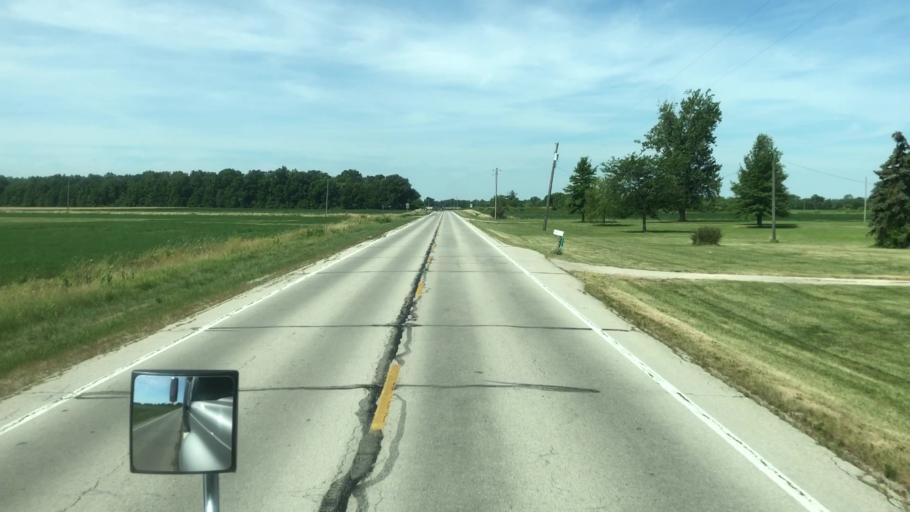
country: US
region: Ohio
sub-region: Sandusky County
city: Clyde
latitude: 41.4034
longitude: -82.9951
